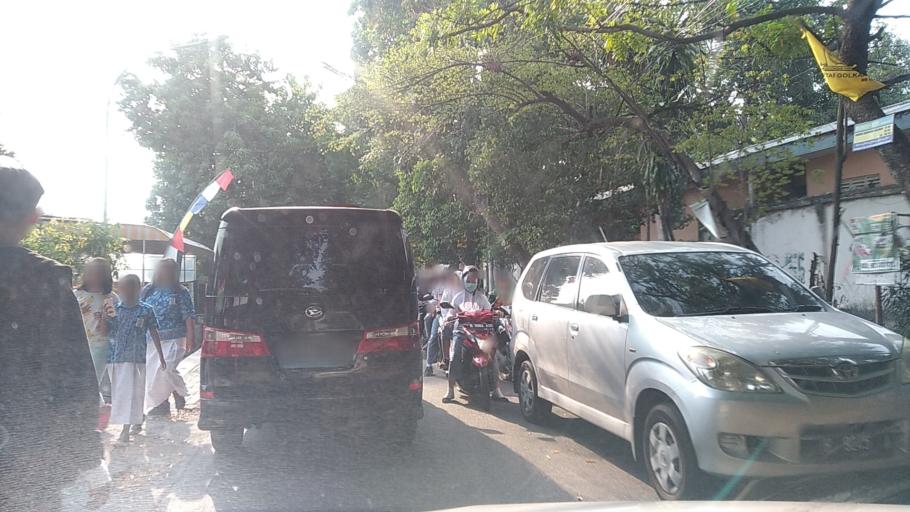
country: ID
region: Central Java
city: Semarang
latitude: -7.0003
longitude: 110.4302
